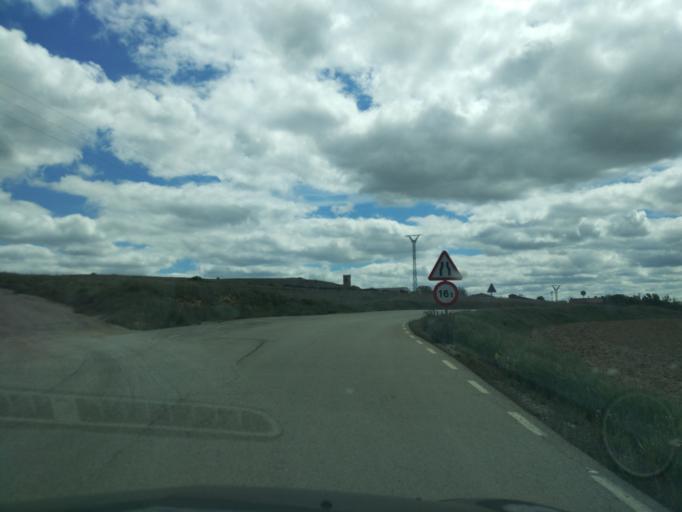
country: ES
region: Castille-La Mancha
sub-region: Provincia de Guadalajara
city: Torremocha del Campo
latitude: 40.9834
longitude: -2.5967
